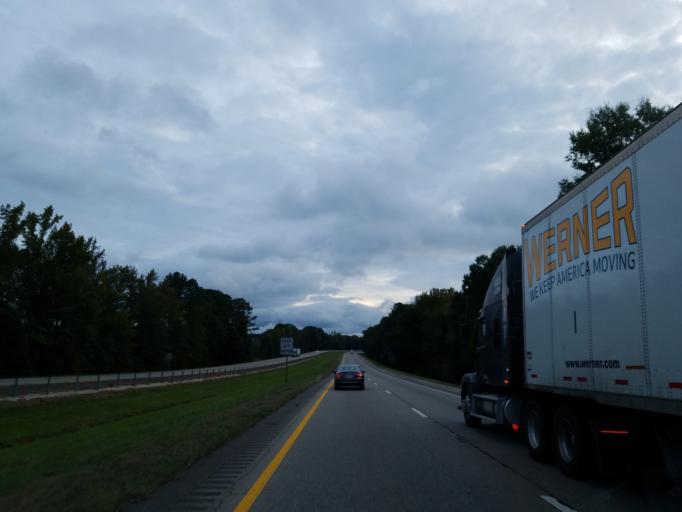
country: US
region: Alabama
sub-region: Sumter County
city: York
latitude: 32.4198
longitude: -88.4565
